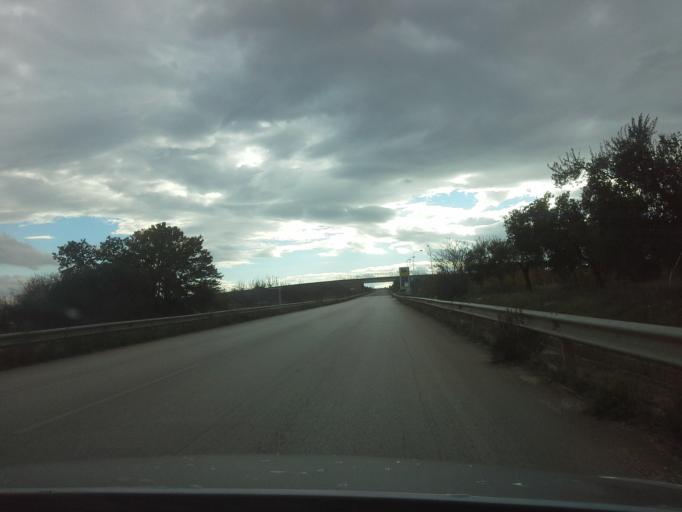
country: IT
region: Apulia
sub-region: Provincia di Bari
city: Turi
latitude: 40.9179
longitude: 16.9982
